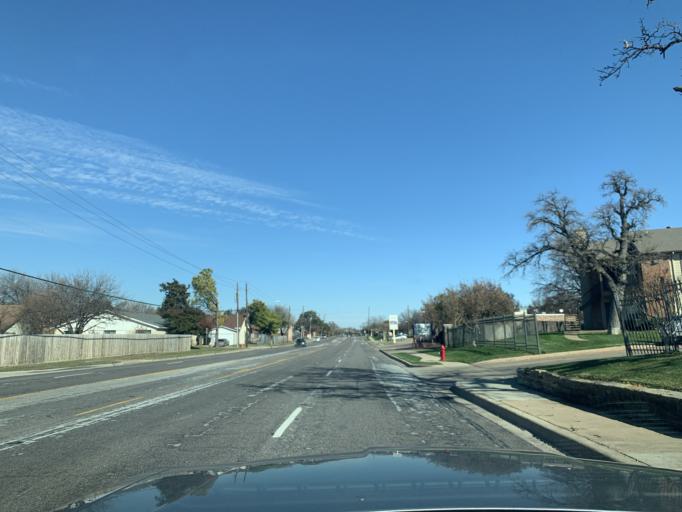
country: US
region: Texas
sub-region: Tarrant County
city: Bedford
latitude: 32.8405
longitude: -97.1484
